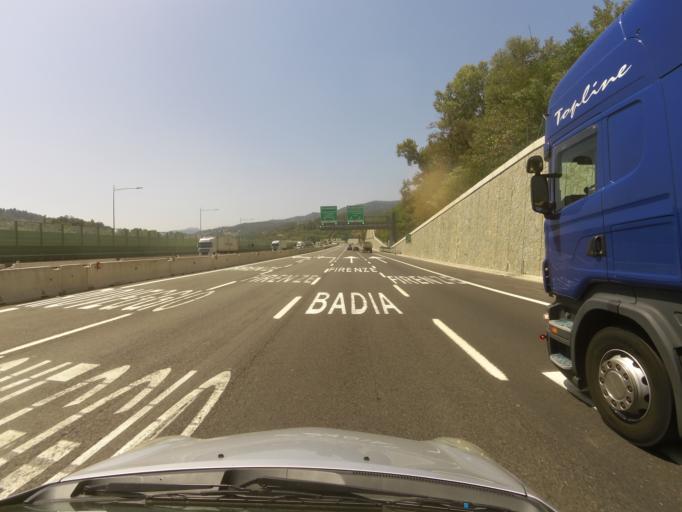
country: IT
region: Emilia-Romagna
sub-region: Provincia di Bologna
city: Vado
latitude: 44.2945
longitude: 11.2182
